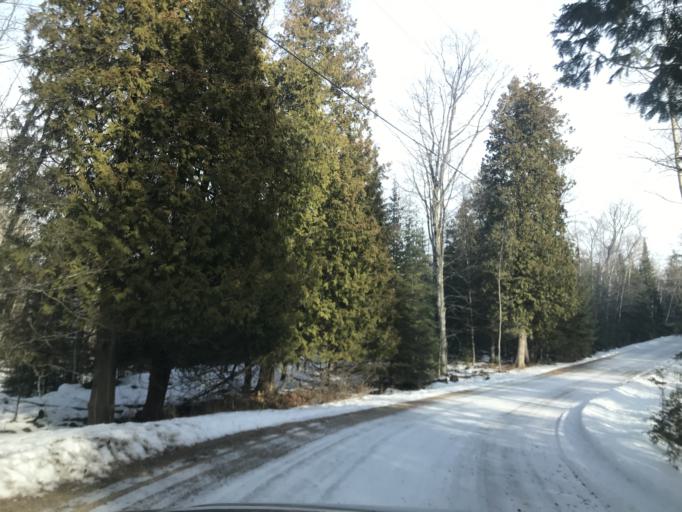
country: US
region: Wisconsin
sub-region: Door County
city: Sturgeon Bay
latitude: 45.1547
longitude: -87.0488
